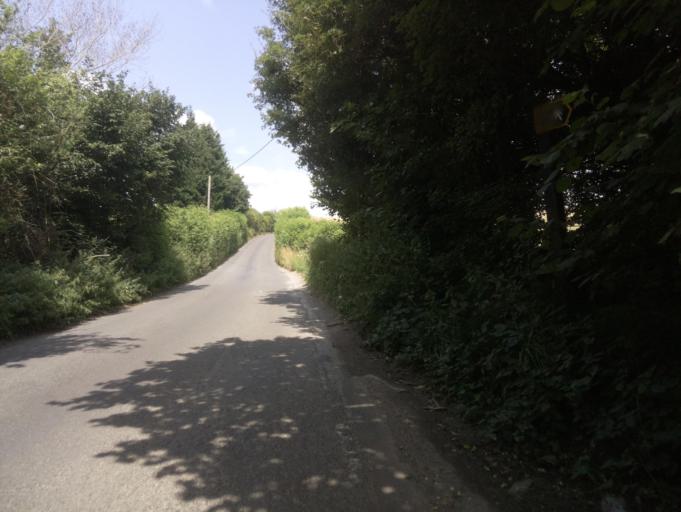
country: GB
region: England
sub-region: Wiltshire
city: Purton
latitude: 51.5753
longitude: -1.8653
